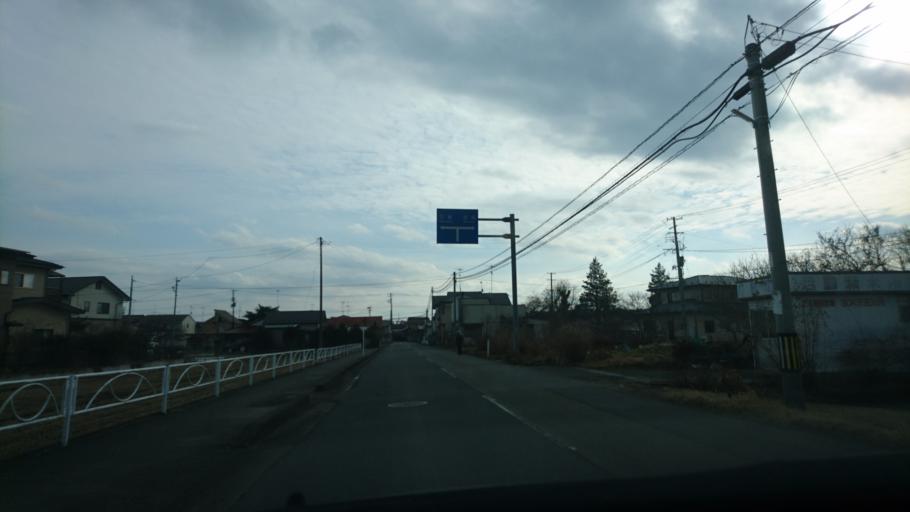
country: JP
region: Iwate
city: Ichinoseki
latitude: 38.8493
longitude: 141.1721
